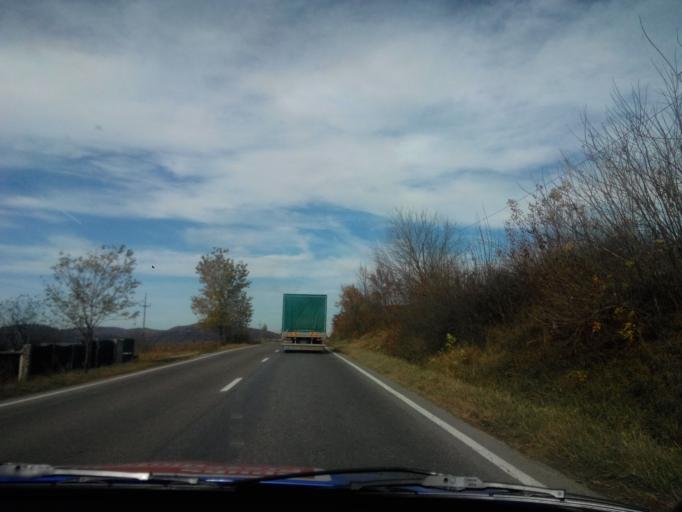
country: RO
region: Bacau
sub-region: Comuna Helegiu
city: Helegiu
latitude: 46.3719
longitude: 26.7346
